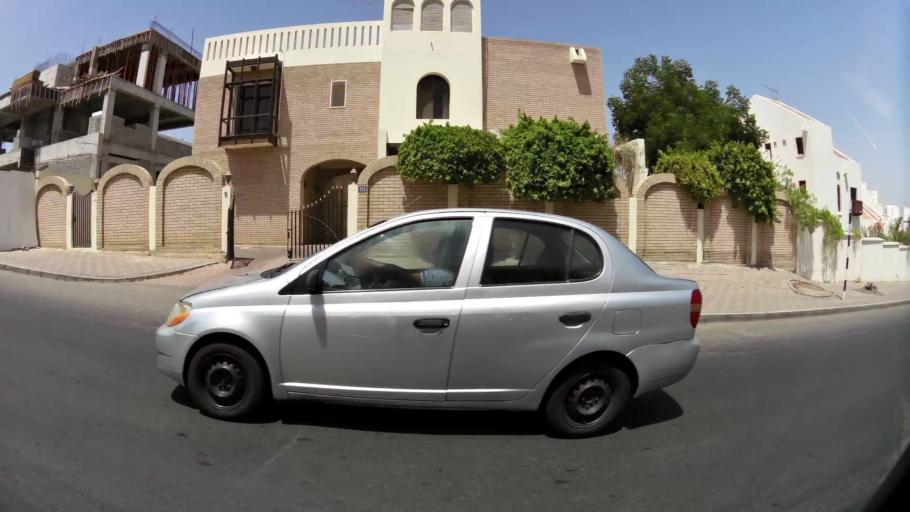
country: OM
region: Muhafazat Masqat
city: Muscat
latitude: 23.6237
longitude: 58.4867
